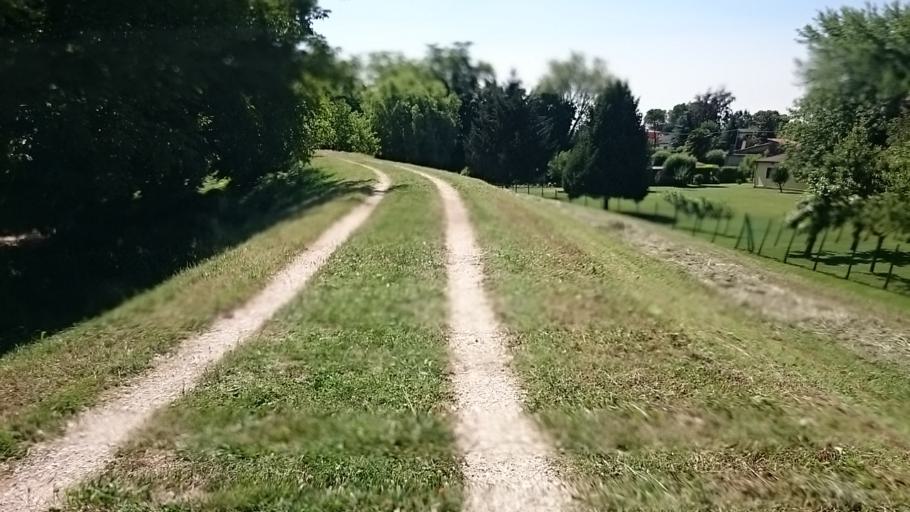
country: IT
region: Veneto
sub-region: Provincia di Padova
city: Saccolongo
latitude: 45.3952
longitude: 11.7677
